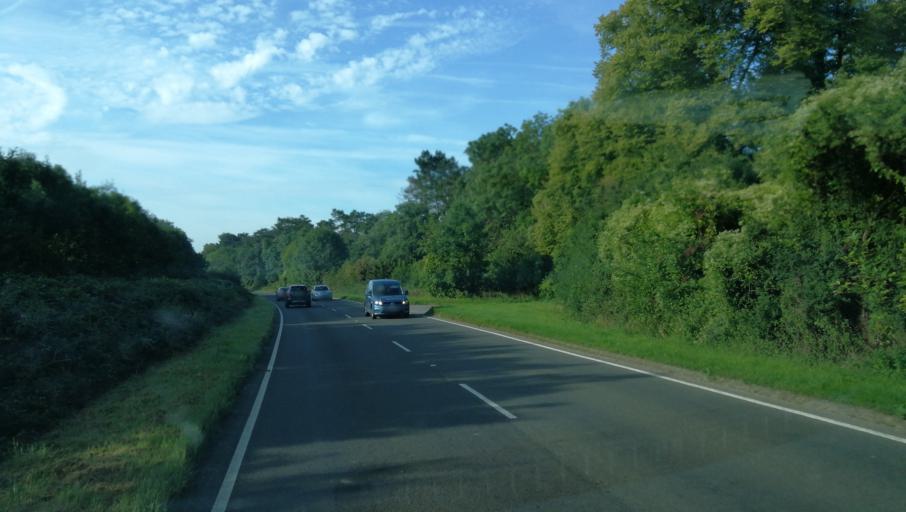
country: GB
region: England
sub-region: Oxfordshire
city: Somerton
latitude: 51.9122
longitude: -1.3282
